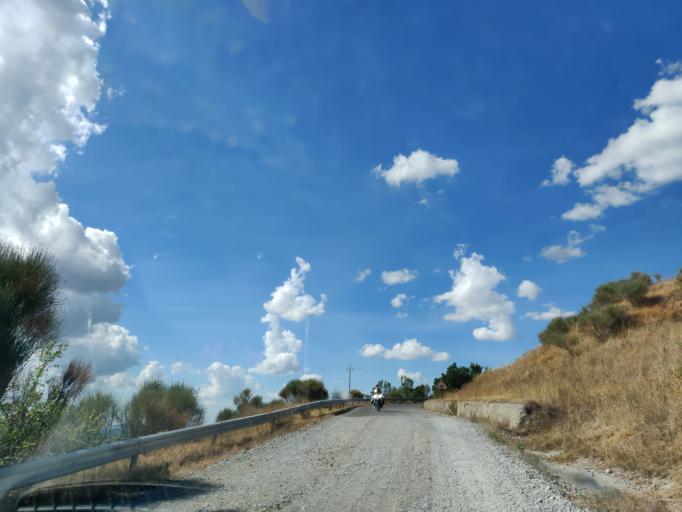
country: IT
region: Tuscany
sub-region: Provincia di Siena
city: Radicofani
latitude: 42.9398
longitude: 11.7335
